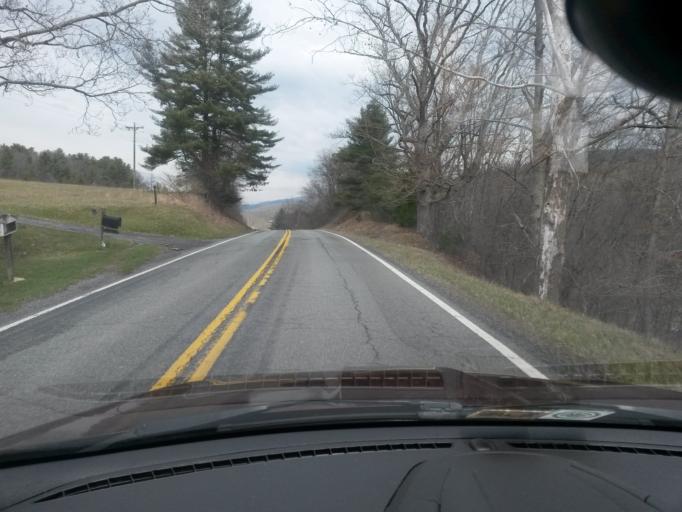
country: US
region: Virginia
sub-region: Highland County
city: Monterey
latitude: 38.2434
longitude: -79.6814
